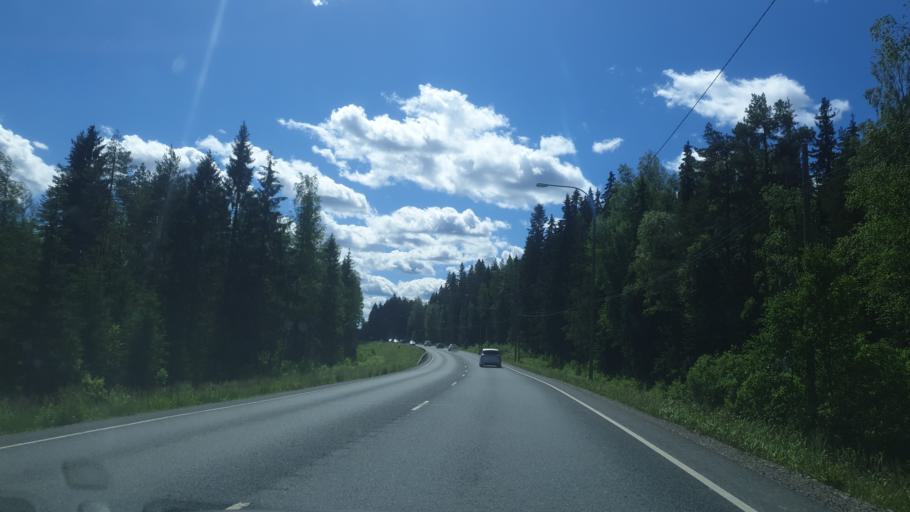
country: FI
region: Northern Savo
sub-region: Varkaus
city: Leppaevirta
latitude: 62.5572
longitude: 27.6196
